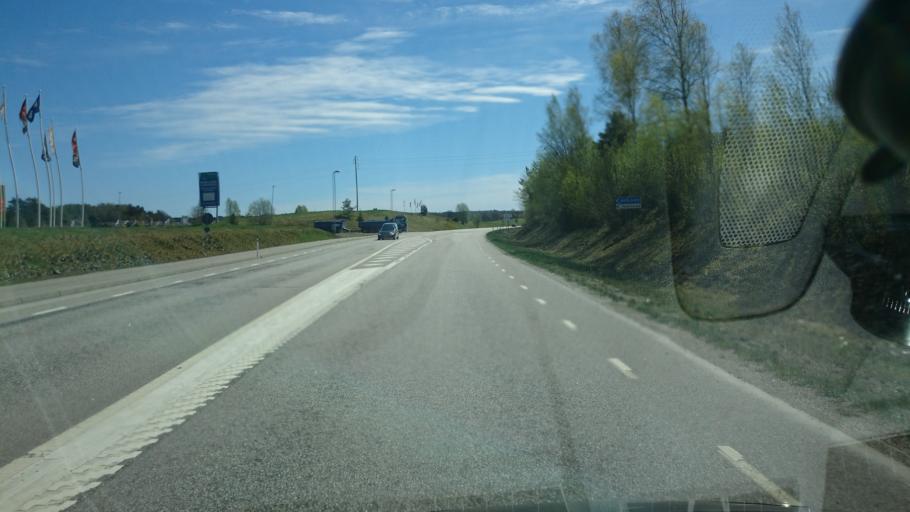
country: SE
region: Vaestra Goetaland
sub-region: Munkedals Kommun
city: Munkedal
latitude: 58.4774
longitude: 11.6533
